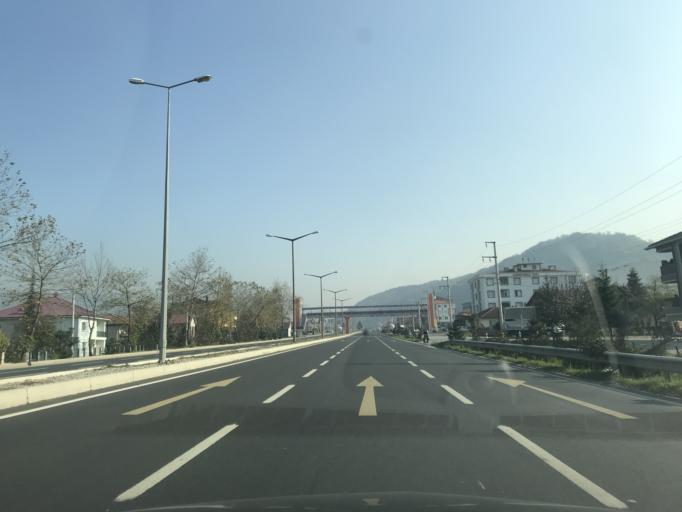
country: TR
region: Duzce
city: Kaynasli
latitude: 40.7744
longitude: 31.3134
